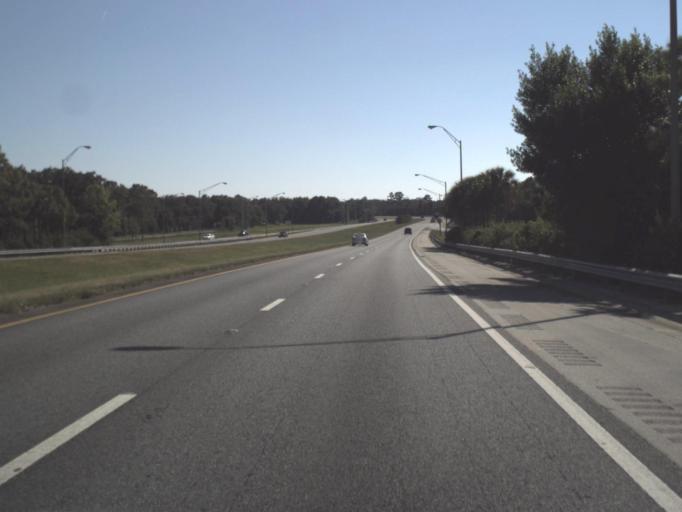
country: US
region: Florida
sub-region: Seminole County
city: Goldenrod
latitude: 28.6171
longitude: -81.2588
